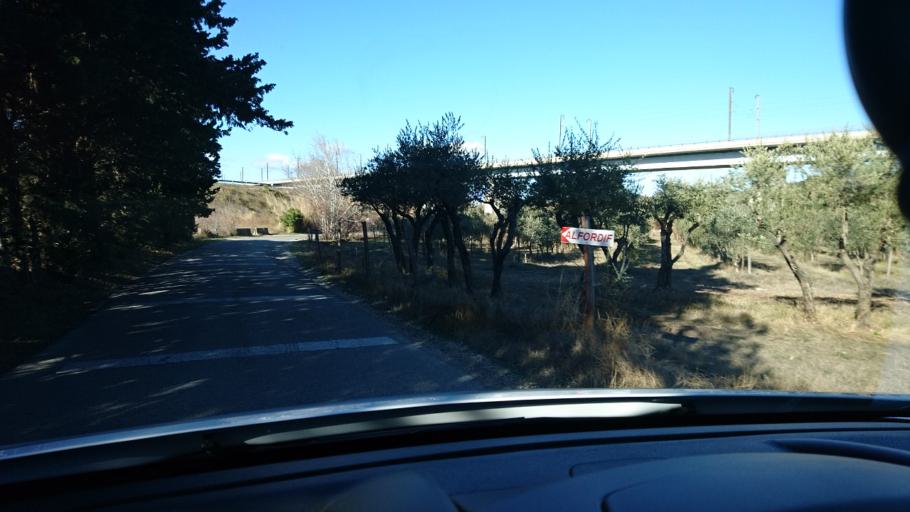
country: FR
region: Provence-Alpes-Cote d'Azur
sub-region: Departement du Vaucluse
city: Caumont-sur-Durance
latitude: 43.8903
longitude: 4.9232
